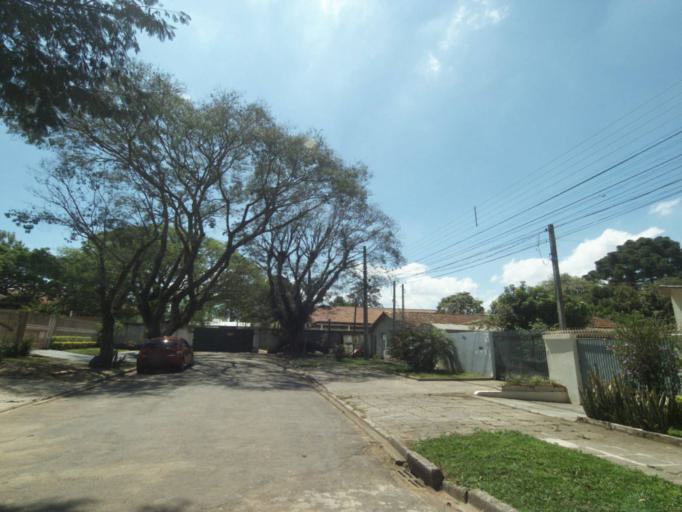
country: BR
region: Parana
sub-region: Curitiba
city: Curitiba
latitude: -25.4054
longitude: -49.2396
